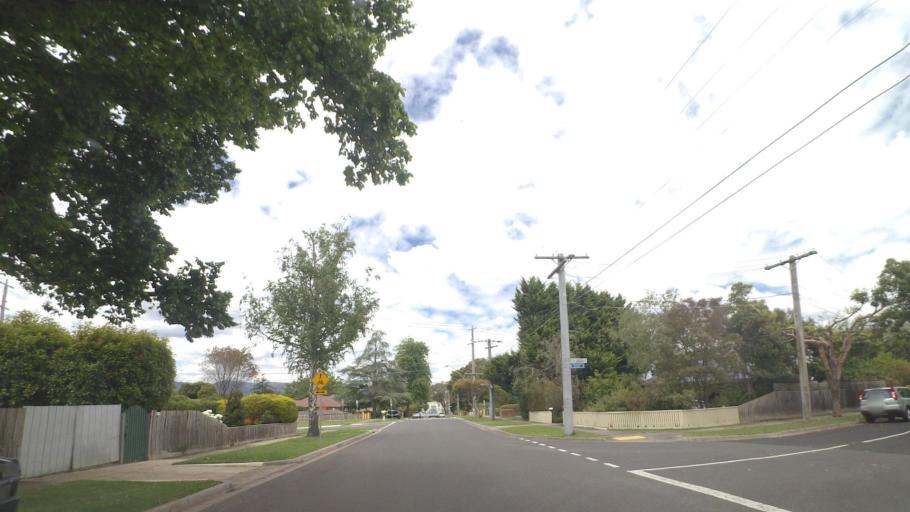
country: AU
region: Victoria
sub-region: Yarra Ranges
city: Kilsyth
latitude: -37.7990
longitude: 145.3044
